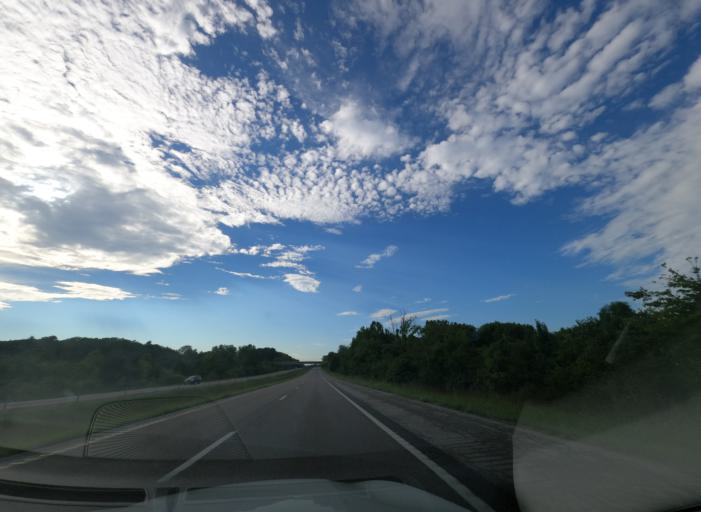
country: US
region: Missouri
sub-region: Jefferson County
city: Crystal City
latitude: 38.1373
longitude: -90.3257
